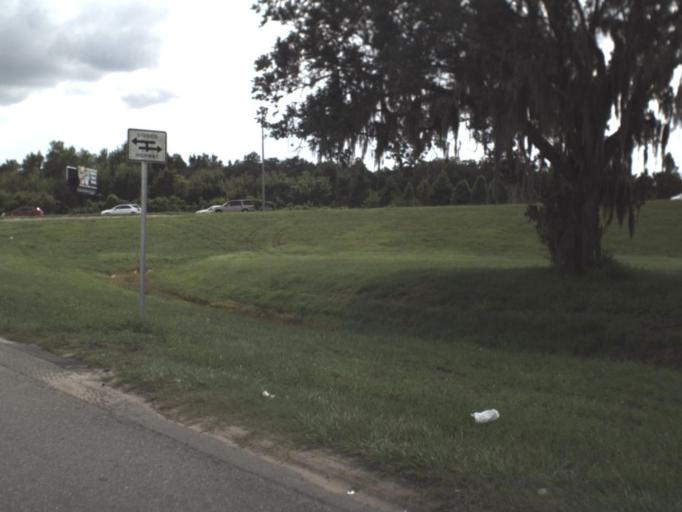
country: US
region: Florida
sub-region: Manatee County
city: Samoset
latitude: 27.4764
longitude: -82.5467
